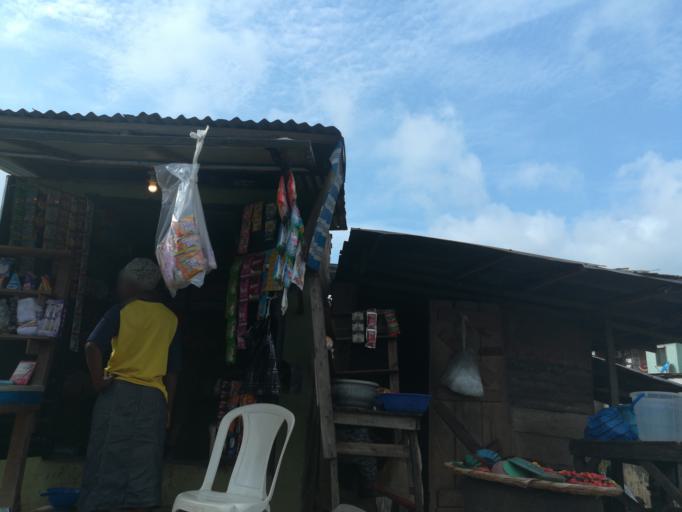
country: NG
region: Lagos
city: Agege
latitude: 6.6135
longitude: 3.3250
